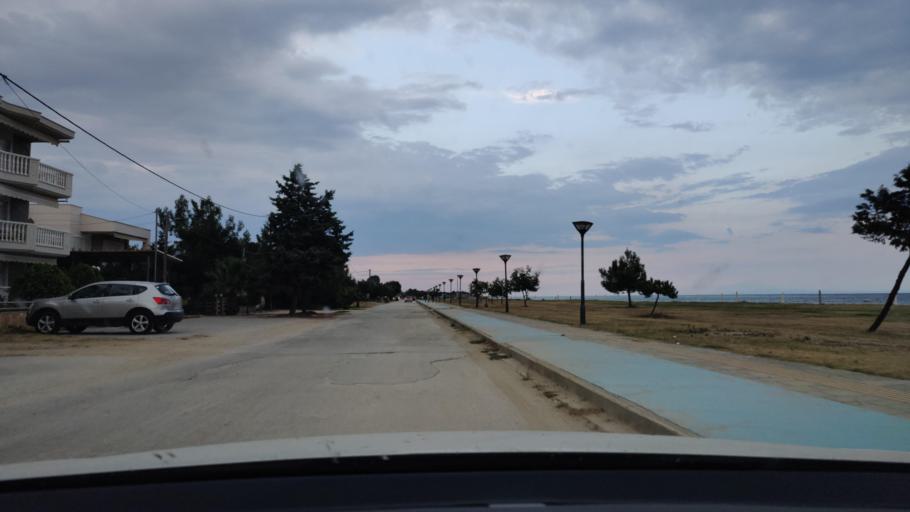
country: GR
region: East Macedonia and Thrace
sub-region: Nomos Kavalas
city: Paralia Ofryniou
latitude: 40.7709
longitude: 23.8882
